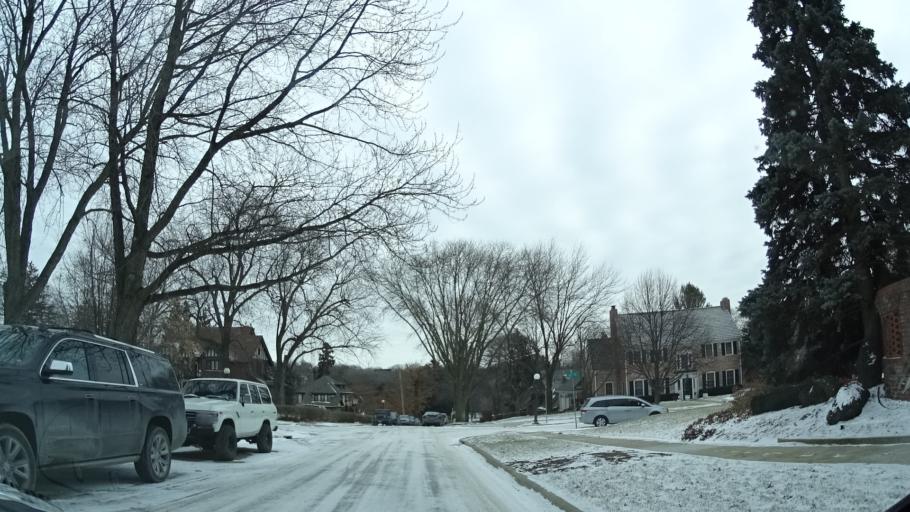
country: US
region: Nebraska
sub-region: Douglas County
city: Omaha
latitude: 41.2666
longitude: -95.9993
